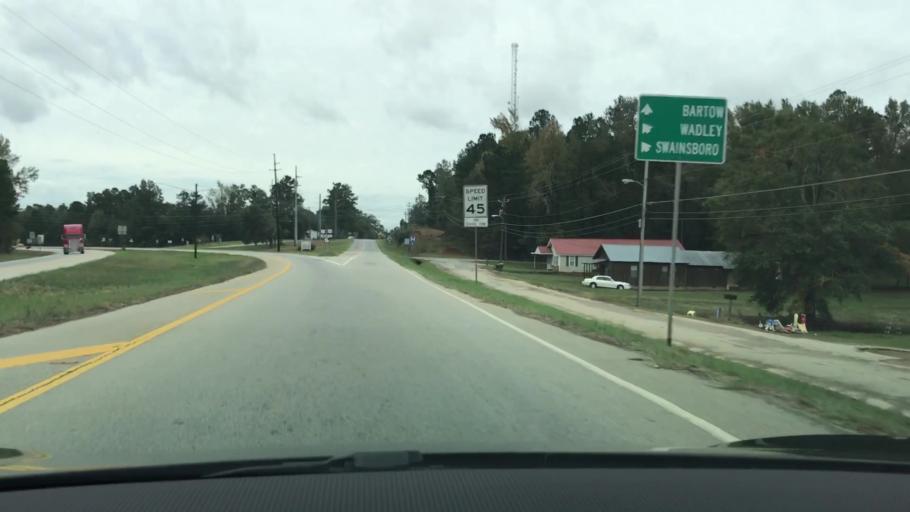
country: US
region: Georgia
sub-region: Jefferson County
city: Louisville
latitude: 33.0176
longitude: -82.4043
